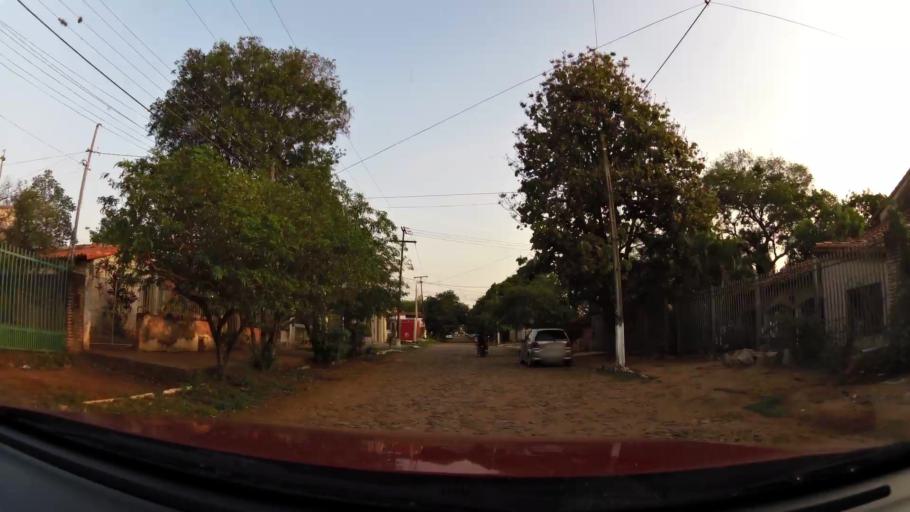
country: PY
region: Central
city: Lambare
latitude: -25.3456
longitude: -57.6004
